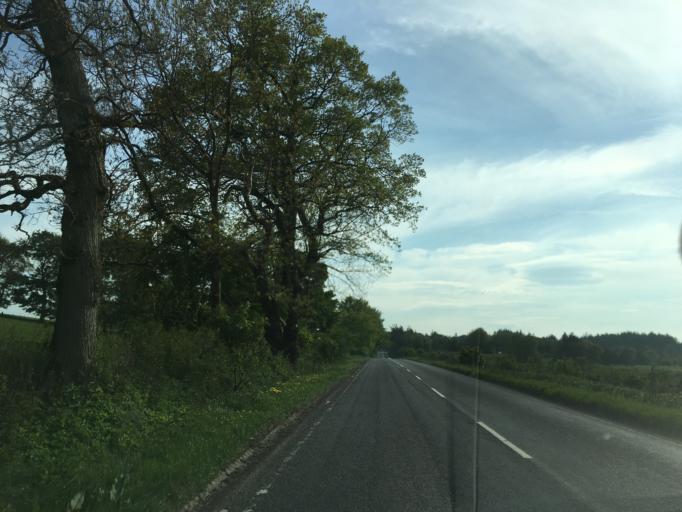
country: GB
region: Scotland
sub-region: Midlothian
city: Penicuik
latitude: 55.7716
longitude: -3.2453
